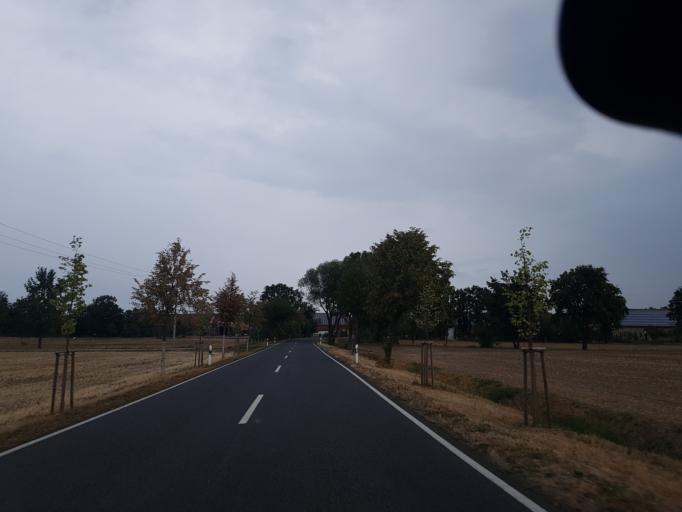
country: DE
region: Saxony-Anhalt
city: Pretzsch
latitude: 51.7509
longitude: 12.8827
